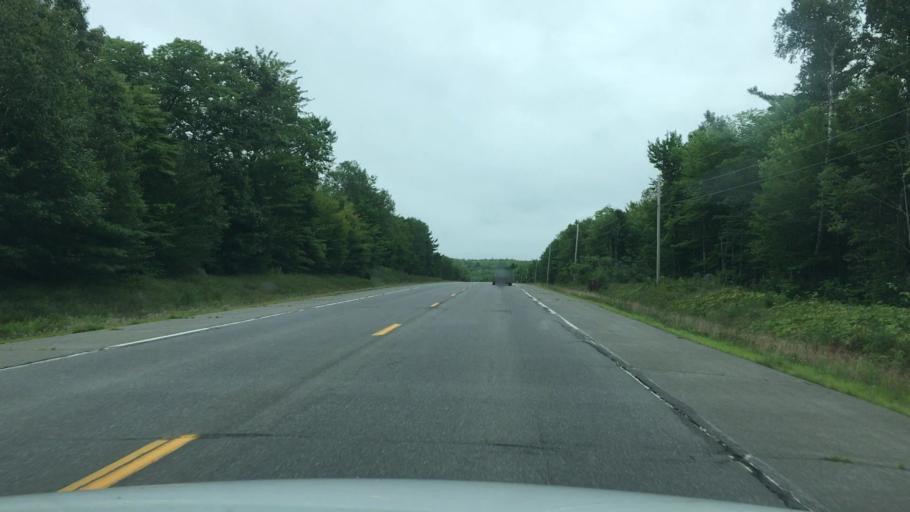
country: US
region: Maine
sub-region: Hancock County
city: Franklin
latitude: 44.8346
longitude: -68.1396
